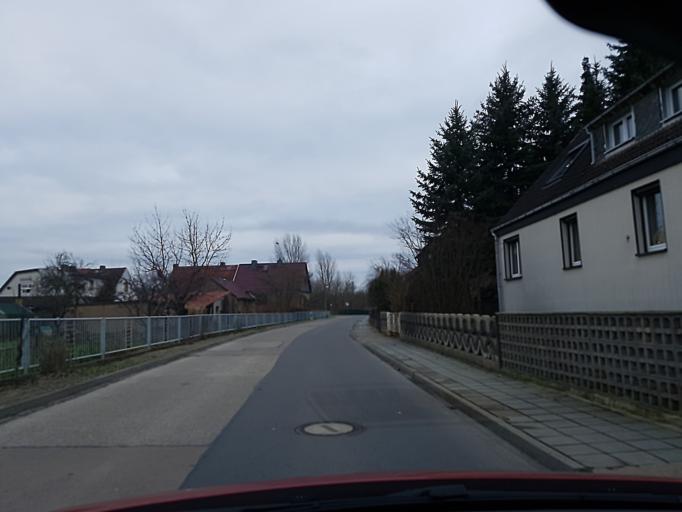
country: DE
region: Brandenburg
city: Elsterwerda
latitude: 51.4584
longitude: 13.5071
